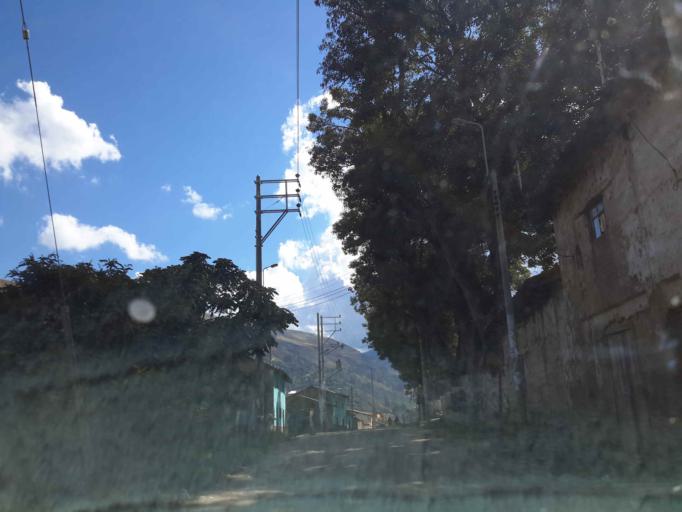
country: PE
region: Apurimac
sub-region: Provincia de Andahuaylas
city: Talavera
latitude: -13.6502
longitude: -73.4390
